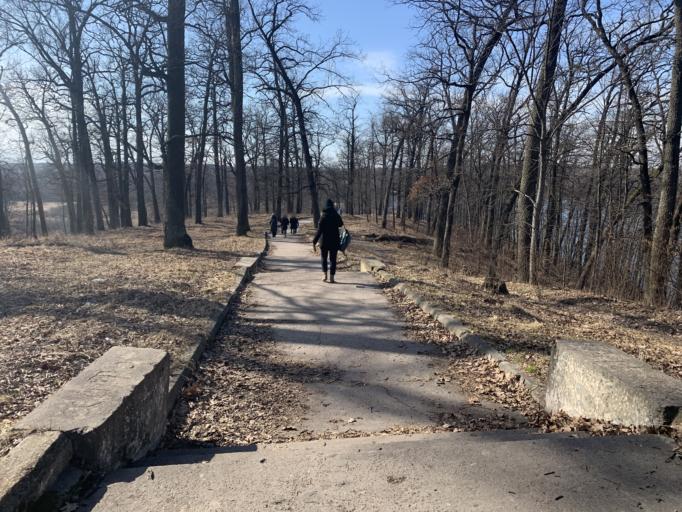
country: RU
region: Kursk
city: Zheleznogorsk
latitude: 52.3197
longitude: 35.3641
